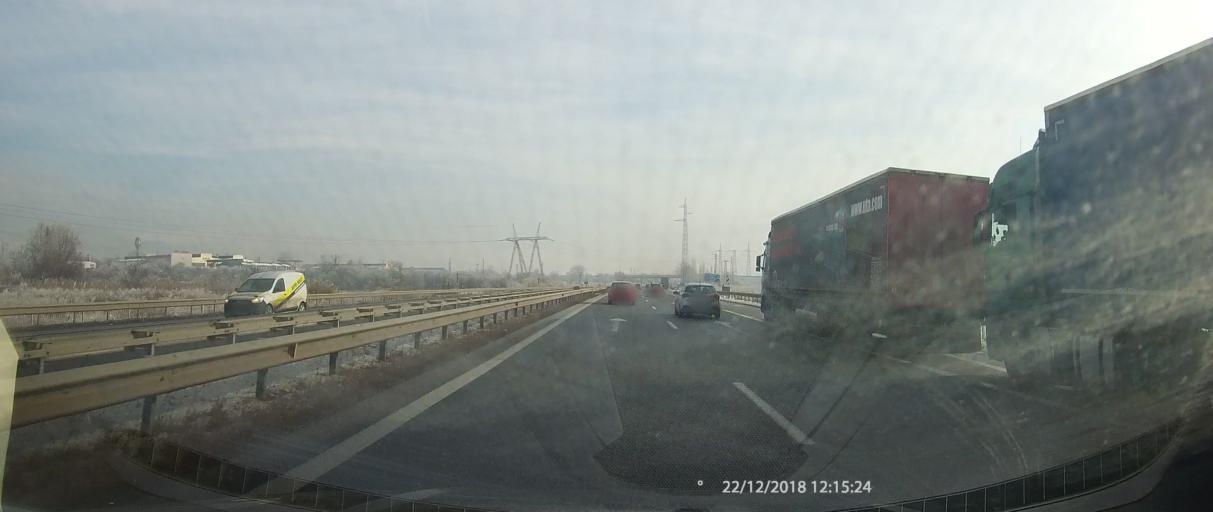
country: BG
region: Sofia-Capital
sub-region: Stolichna Obshtina
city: Bukhovo
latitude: 42.7248
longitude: 23.5413
